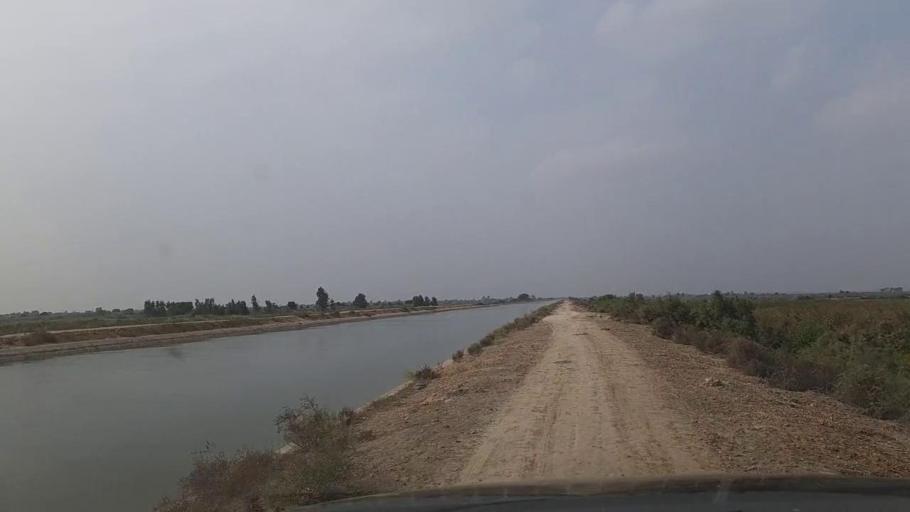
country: PK
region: Sindh
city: Thatta
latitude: 24.8051
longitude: 67.8913
